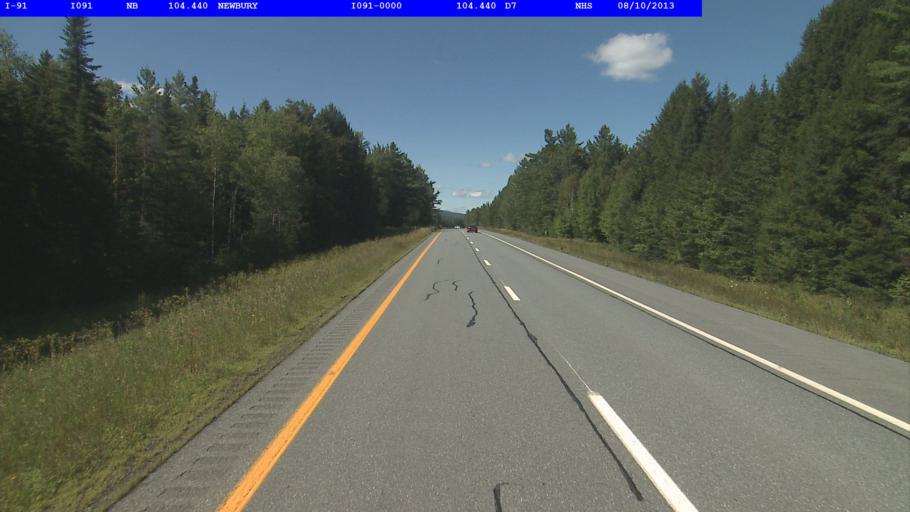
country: US
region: New Hampshire
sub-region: Grafton County
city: Haverhill
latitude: 44.0773
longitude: -72.1114
